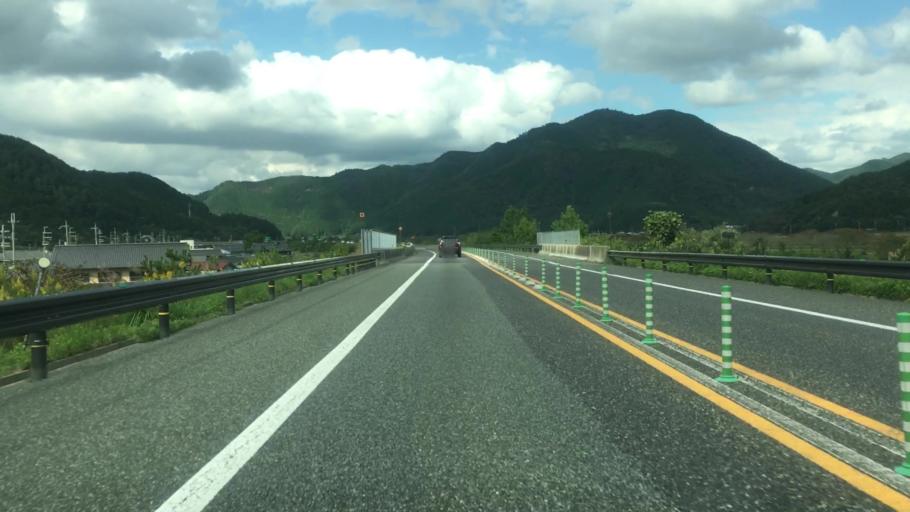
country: JP
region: Kyoto
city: Fukuchiyama
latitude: 35.2187
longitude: 135.0347
